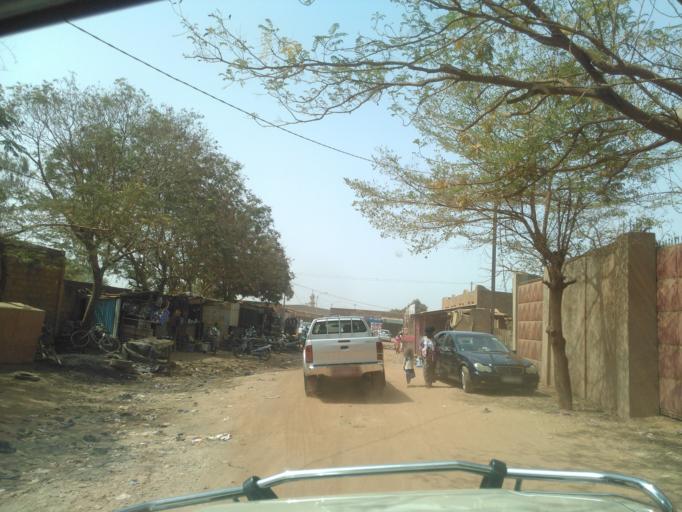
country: BF
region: Centre
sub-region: Kadiogo Province
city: Ouagadougou
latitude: 12.3892
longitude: -1.4764
